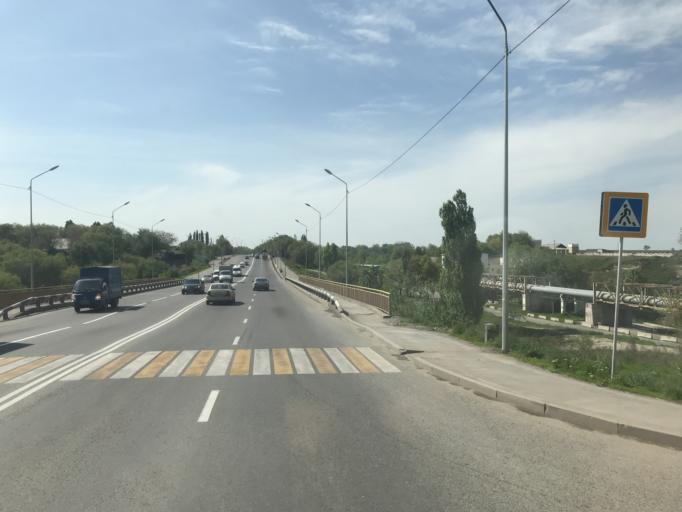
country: KZ
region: Almaty Oblysy
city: Burunday
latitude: 43.3101
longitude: 76.8697
